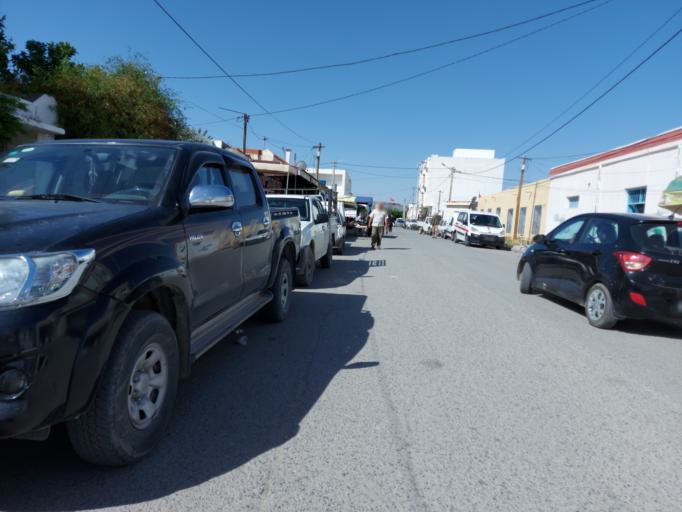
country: TN
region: Silyanah
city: Siliana
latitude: 36.0858
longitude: 9.3690
